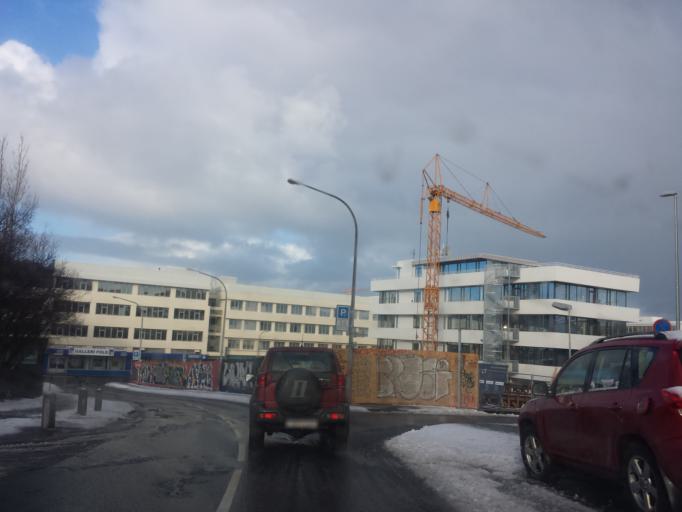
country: IS
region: Capital Region
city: Reykjavik
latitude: 64.1421
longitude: -21.9124
